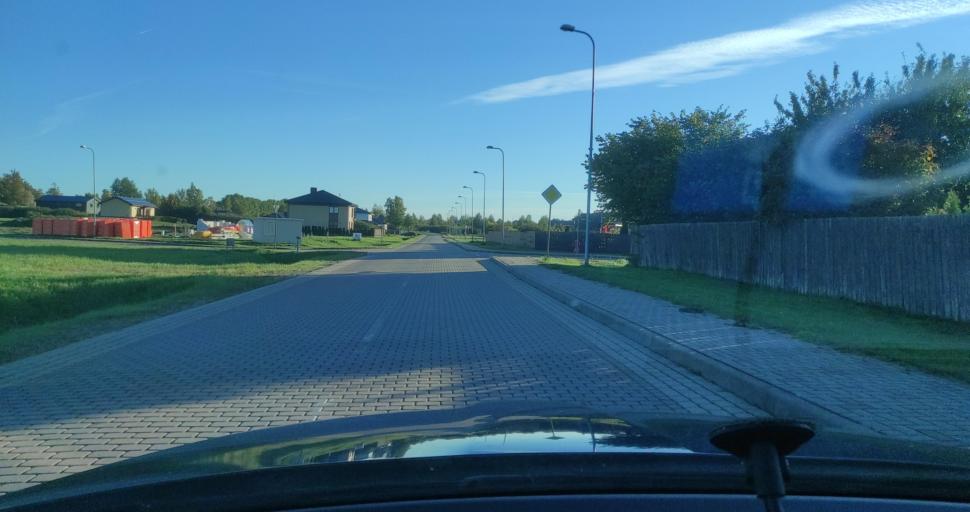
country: LV
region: Ventspils
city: Ventspils
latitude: 57.3681
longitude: 21.5744
